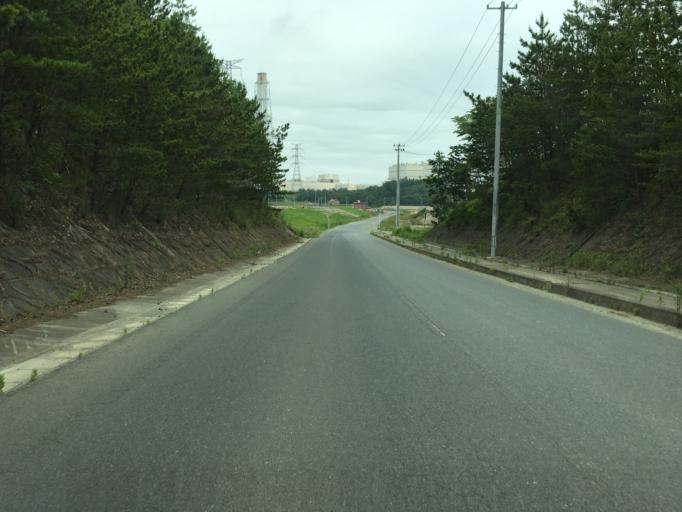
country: JP
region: Fukushima
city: Namie
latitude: 37.6571
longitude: 141.0141
